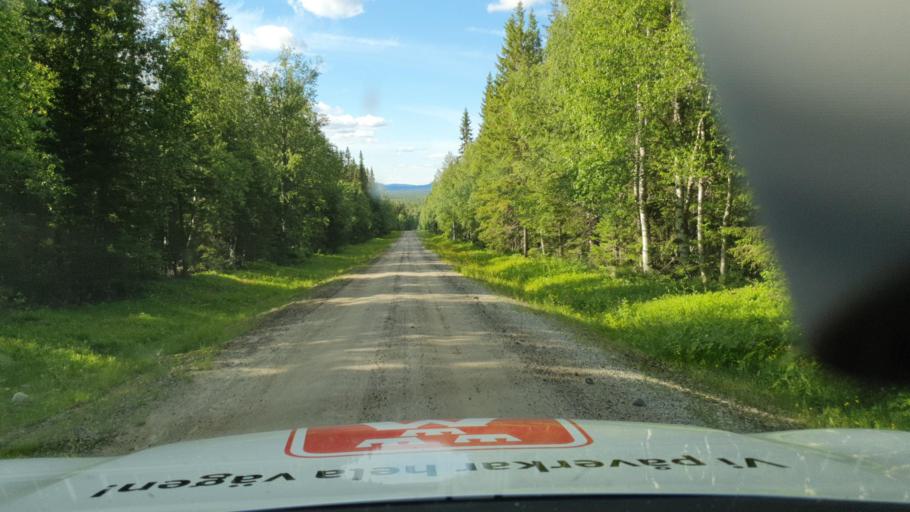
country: SE
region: Vaesterbotten
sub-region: Lycksele Kommun
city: Lycksele
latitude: 64.4244
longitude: 18.2788
